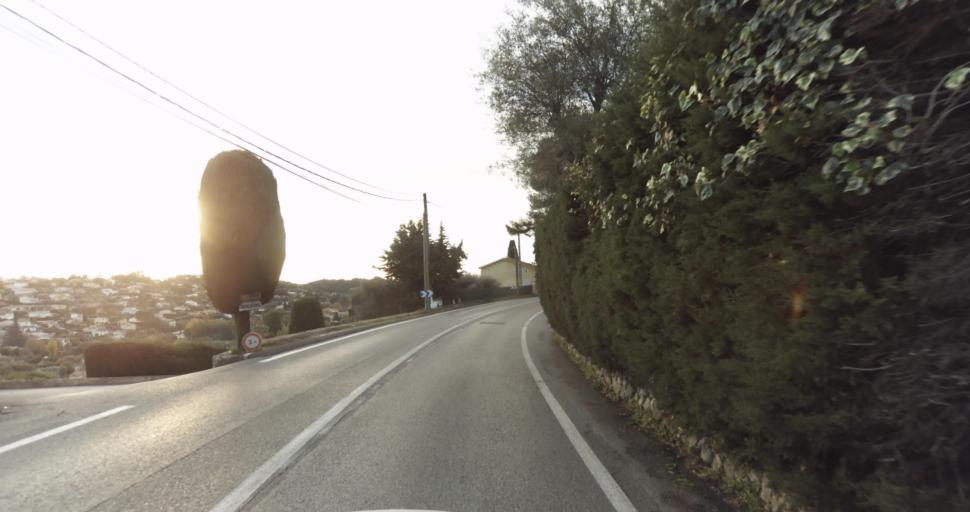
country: FR
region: Provence-Alpes-Cote d'Azur
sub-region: Departement des Alpes-Maritimes
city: Vence
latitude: 43.7171
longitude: 7.1247
